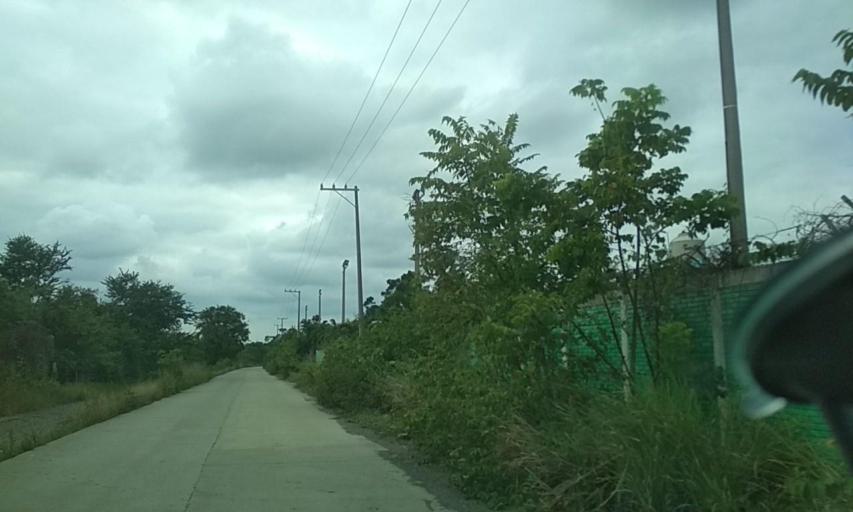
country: MX
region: Veracruz
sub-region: Papantla
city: Polutla
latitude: 20.5423
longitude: -97.2591
